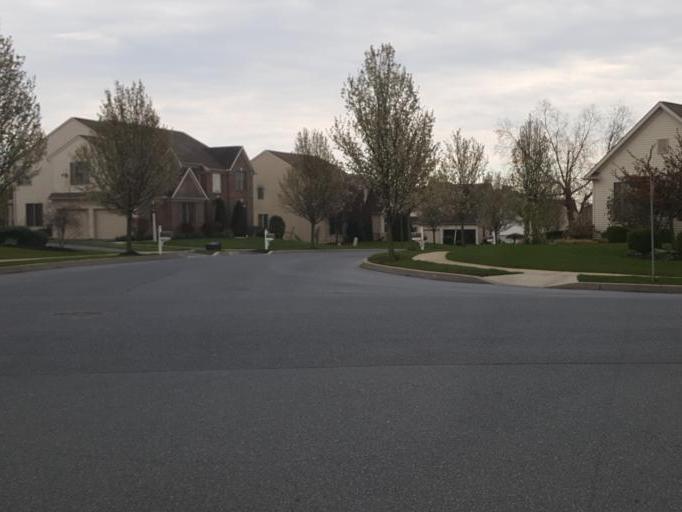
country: US
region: Pennsylvania
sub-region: Dauphin County
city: Hummelstown
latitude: 40.2358
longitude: -76.7220
